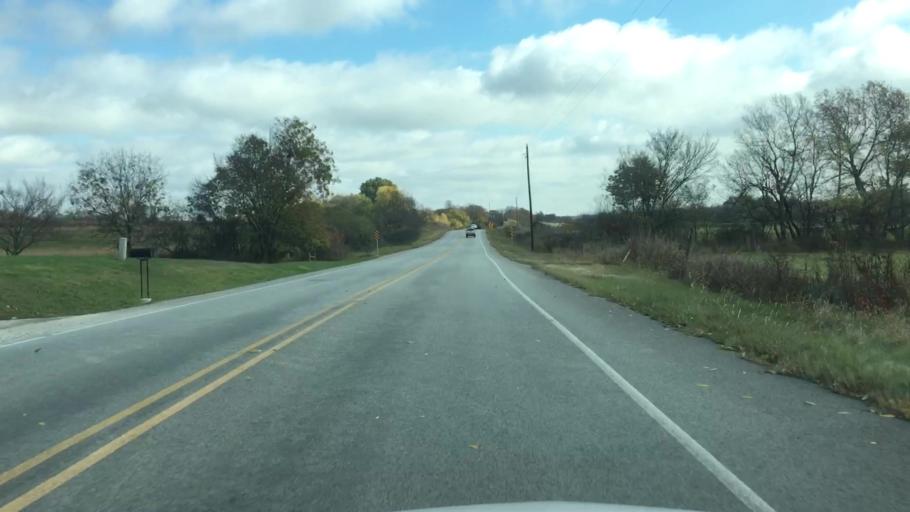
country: US
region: Arkansas
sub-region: Benton County
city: Centerton
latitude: 36.3021
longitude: -94.3137
